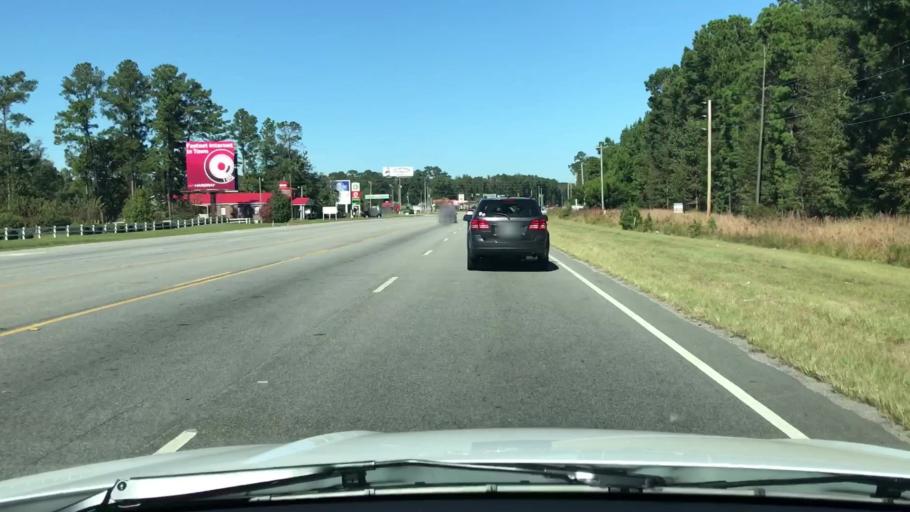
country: US
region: South Carolina
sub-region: Beaufort County
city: Bluffton
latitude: 32.3371
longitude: -80.9283
